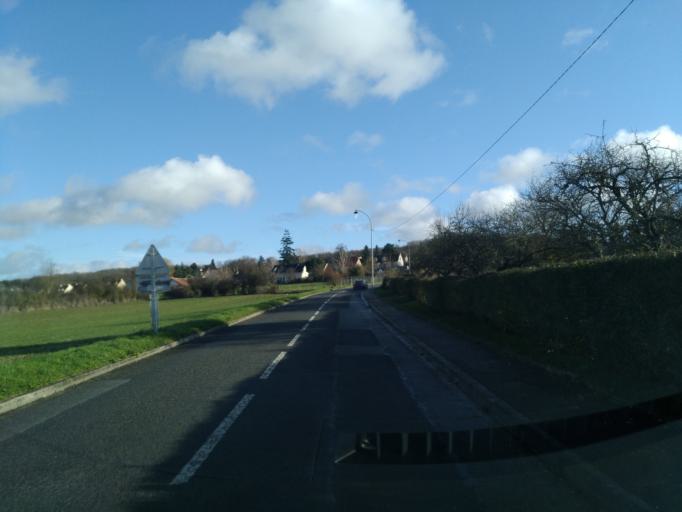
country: FR
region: Ile-de-France
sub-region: Departement des Yvelines
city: Villiers-Saint-Frederic
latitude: 48.8184
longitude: 1.8816
